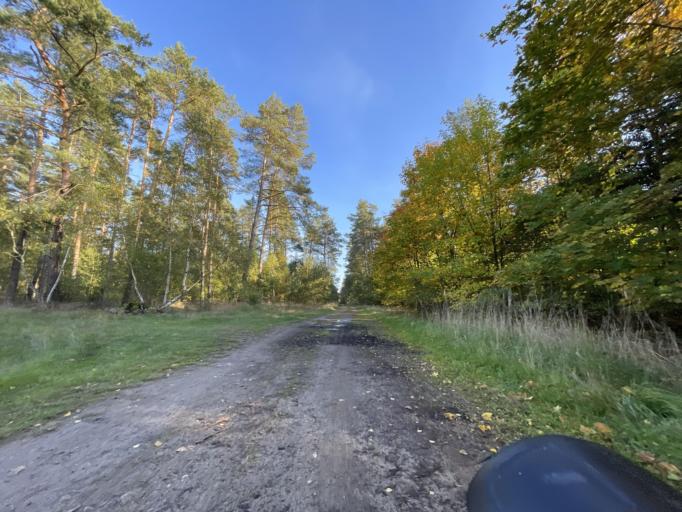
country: DE
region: Lower Saxony
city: Barendorf
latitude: 53.2061
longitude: 10.5041
